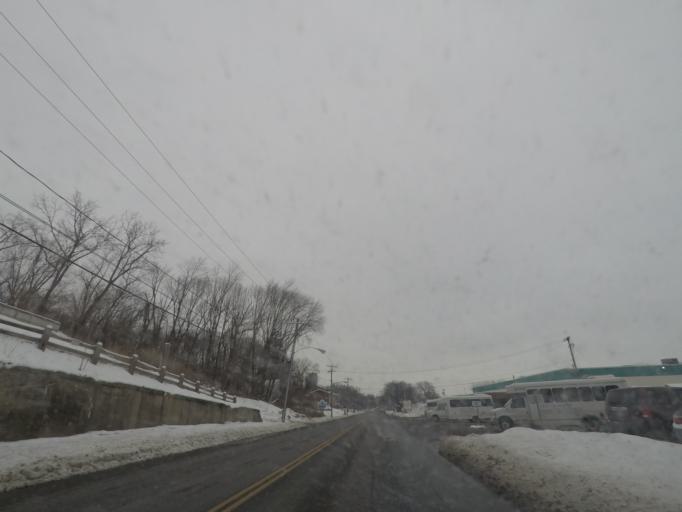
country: US
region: New York
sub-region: Albany County
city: Albany
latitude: 42.6284
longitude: -73.7669
